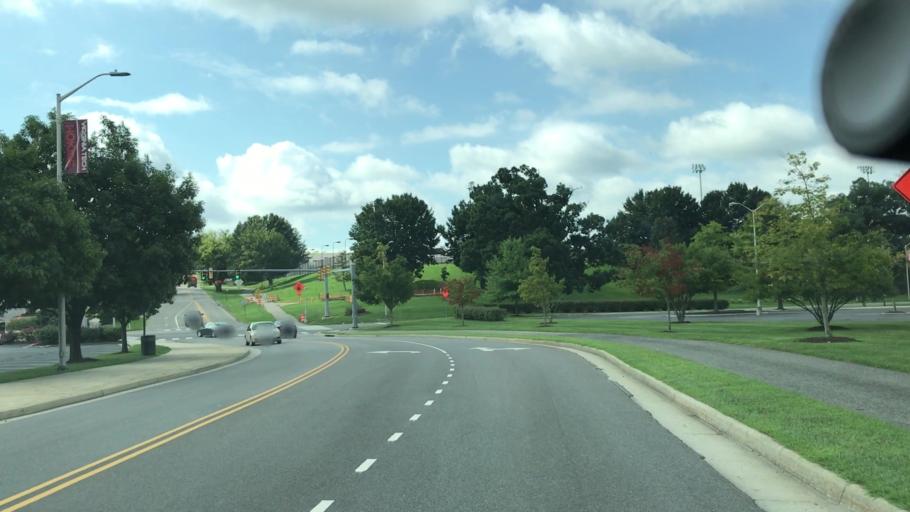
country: US
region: Virginia
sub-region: Montgomery County
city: Blacksburg
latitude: 37.2182
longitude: -80.4193
